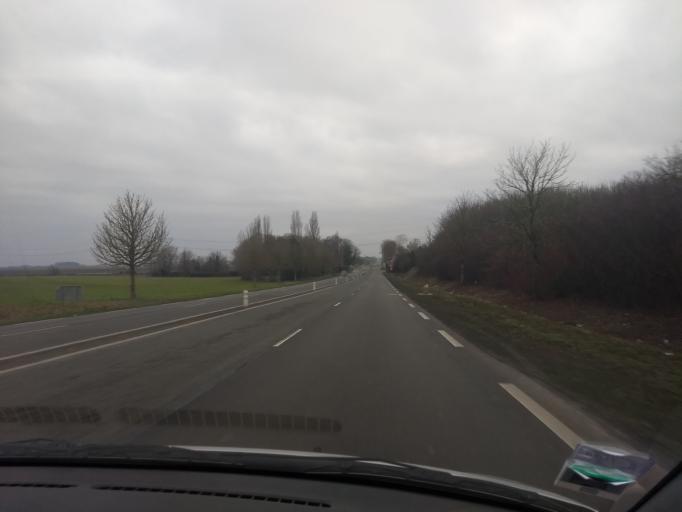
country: FR
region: Nord-Pas-de-Calais
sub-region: Departement du Pas-de-Calais
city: Feuchy
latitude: 50.2705
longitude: 2.8524
